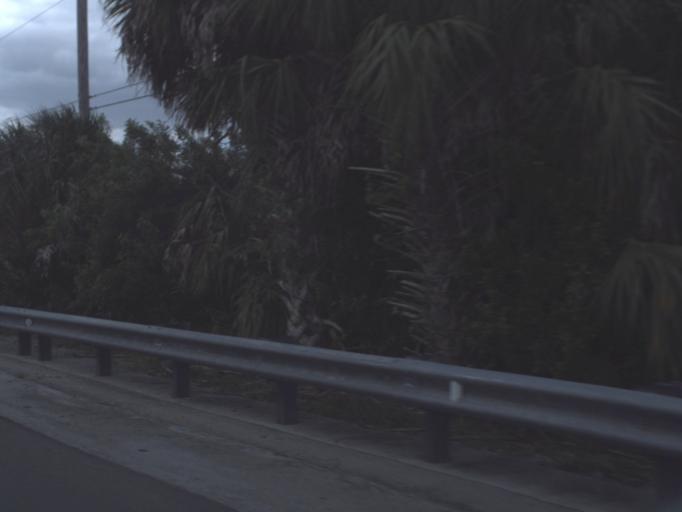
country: US
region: Florida
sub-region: Collier County
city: Marco
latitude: 25.9380
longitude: -81.4610
